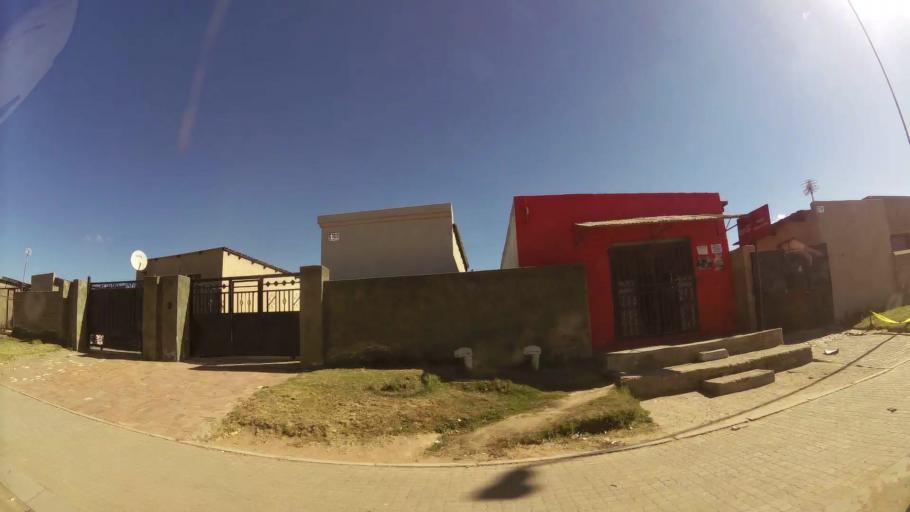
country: ZA
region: Gauteng
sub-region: City of Johannesburg Metropolitan Municipality
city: Midrand
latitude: -25.9221
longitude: 28.0939
